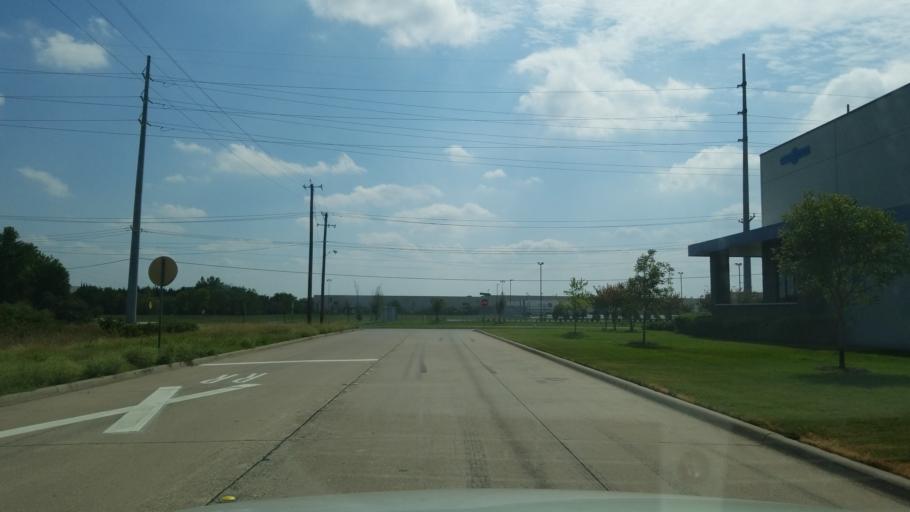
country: US
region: Texas
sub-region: Dallas County
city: Garland
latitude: 32.9019
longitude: -96.6687
